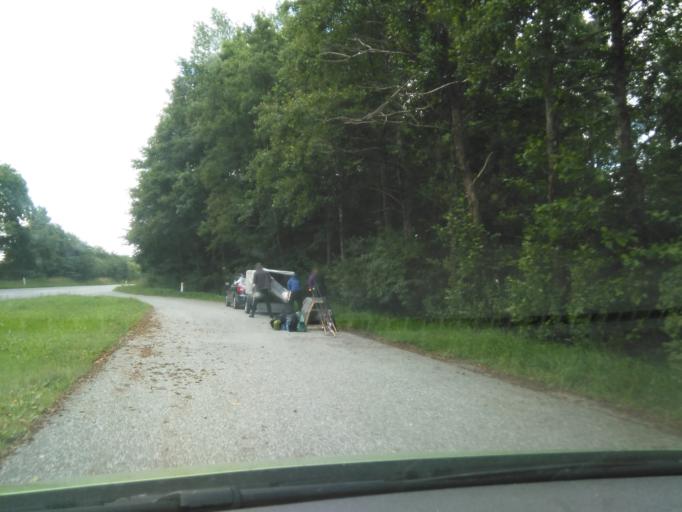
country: DK
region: Central Jutland
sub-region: Arhus Kommune
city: Solbjerg
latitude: 56.0411
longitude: 10.0787
